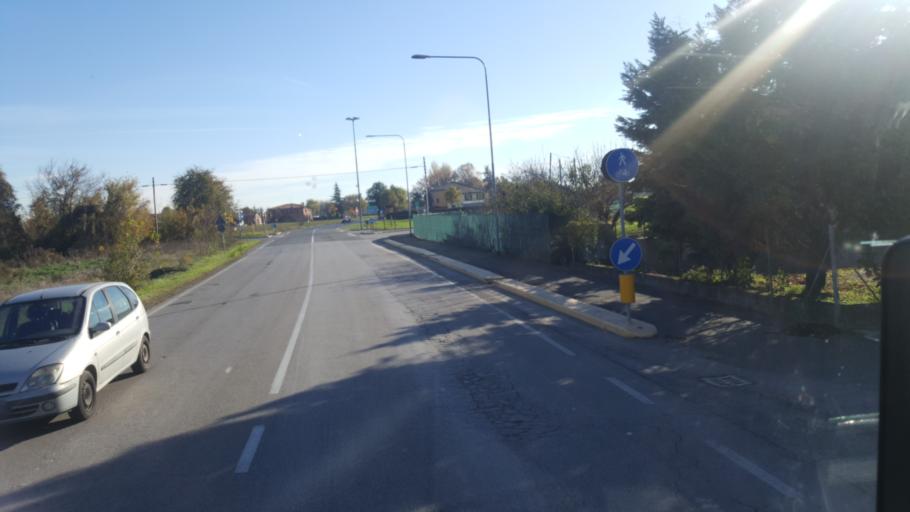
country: IT
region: Emilia-Romagna
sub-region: Provincia di Bologna
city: Calderara di Reno
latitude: 44.5521
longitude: 11.2900
